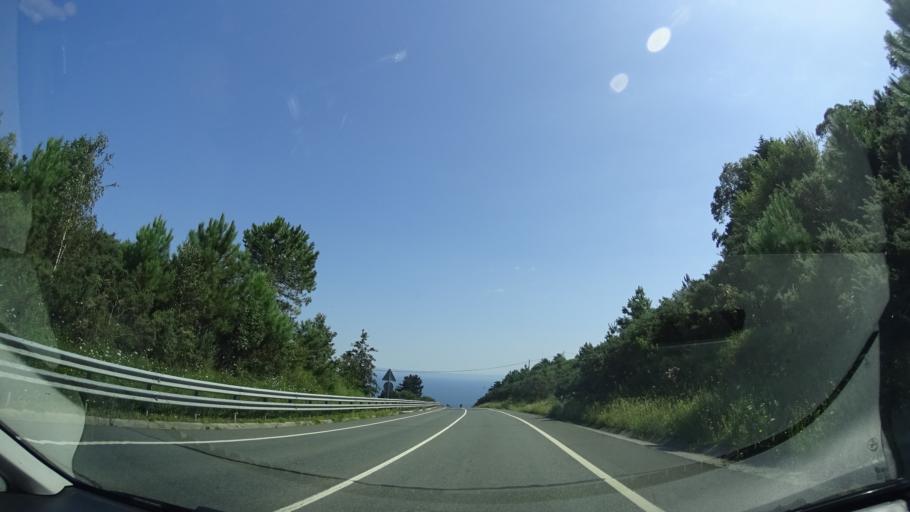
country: ES
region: Basque Country
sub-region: Bizkaia
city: Bakio
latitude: 43.4421
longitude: -2.7680
